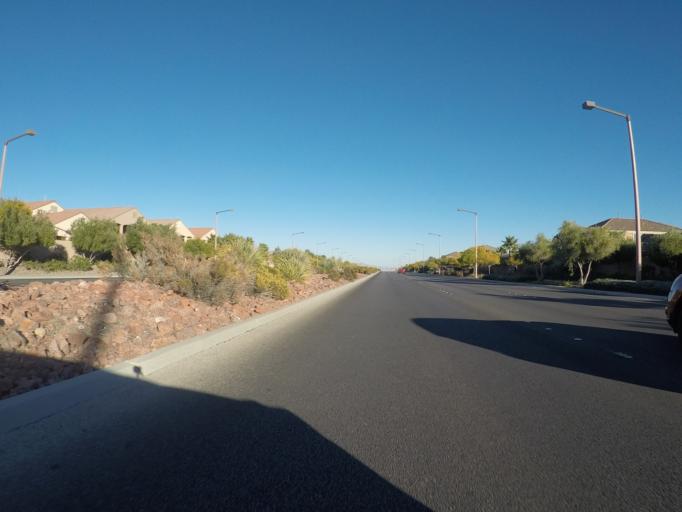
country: US
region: Nevada
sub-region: Clark County
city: Summerlin South
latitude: 36.1589
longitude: -115.3497
